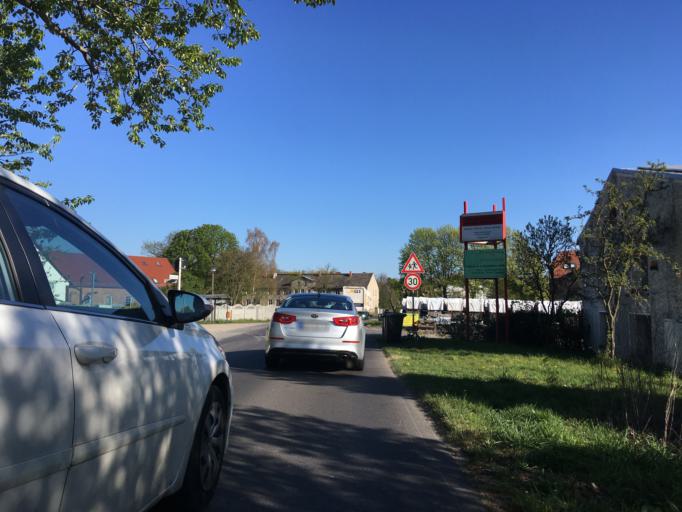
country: DE
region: Brandenburg
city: Bernau bei Berlin
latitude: 52.6904
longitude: 13.5498
